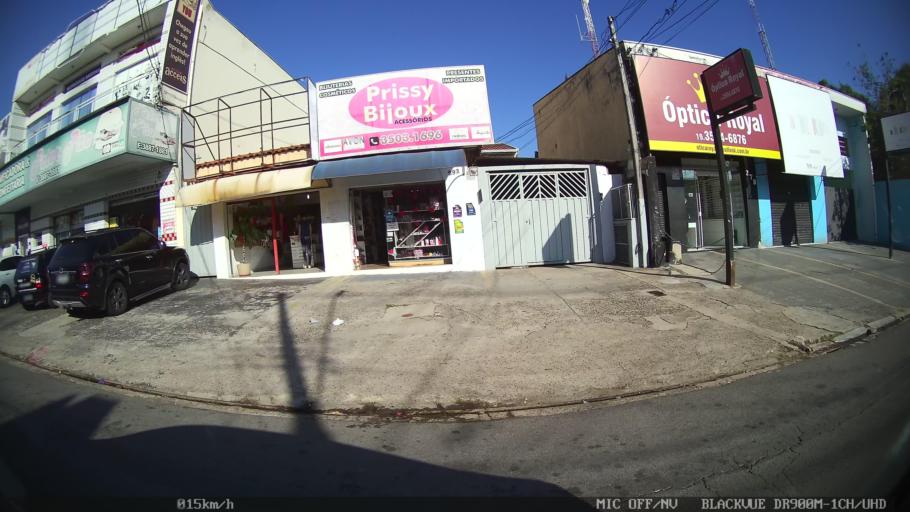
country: BR
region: Sao Paulo
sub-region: Hortolandia
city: Hortolandia
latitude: -22.8952
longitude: -47.1754
